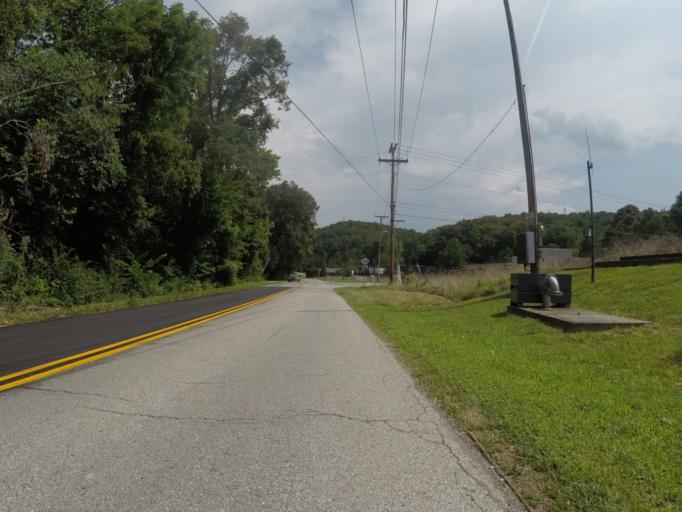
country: US
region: Kentucky
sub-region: Boyd County
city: Ironville
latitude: 38.4471
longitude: -82.6887
